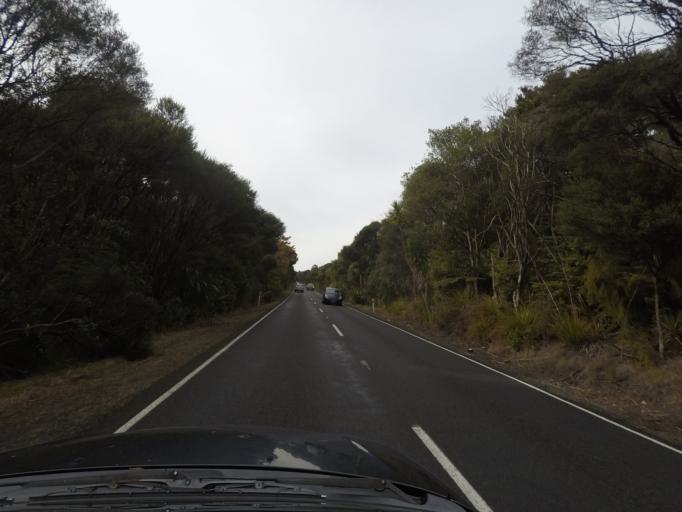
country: NZ
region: Auckland
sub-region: Auckland
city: Titirangi
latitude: -36.9355
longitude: 174.5613
